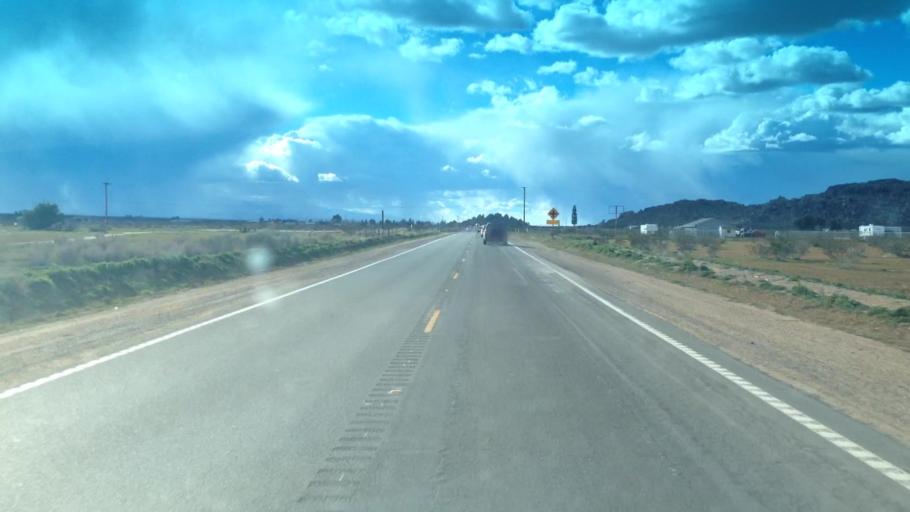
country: US
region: California
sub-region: San Bernardino County
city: Apple Valley
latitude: 34.4719
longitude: -117.1003
